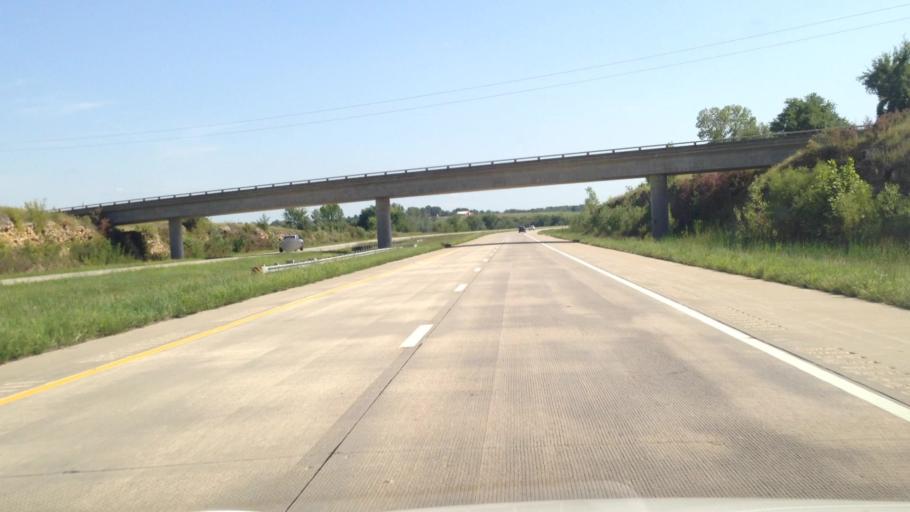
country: US
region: Kansas
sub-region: Miami County
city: Louisburg
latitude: 38.5495
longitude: -94.6881
